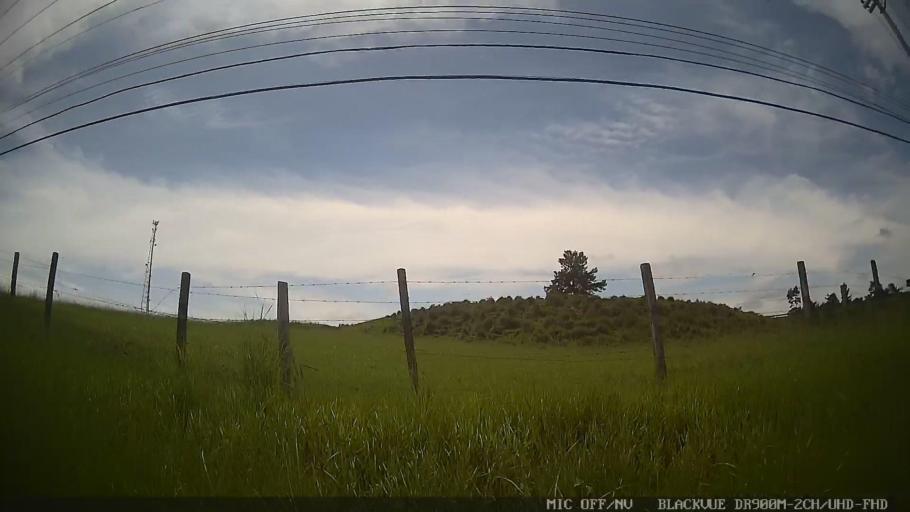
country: BR
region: Sao Paulo
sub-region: Santa Isabel
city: Santa Isabel
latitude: -23.3933
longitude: -46.1737
